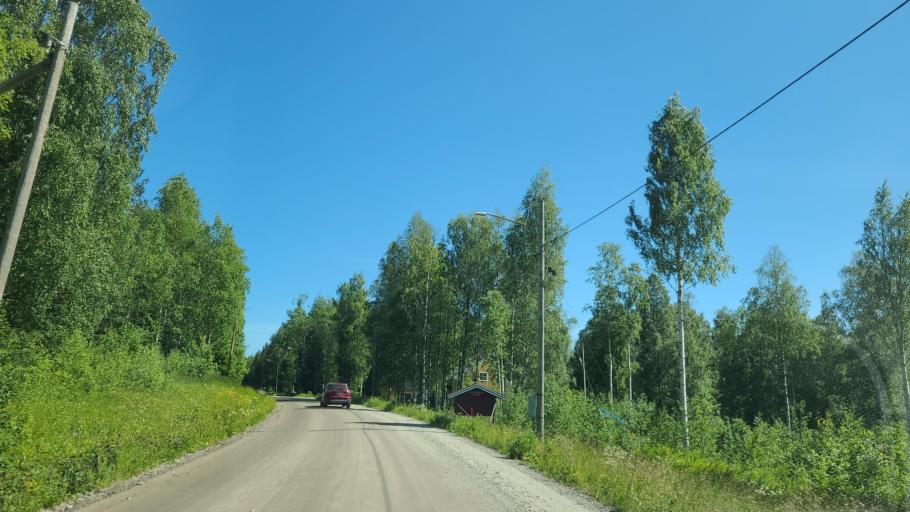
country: SE
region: Vaesterbotten
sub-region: Bjurholms Kommun
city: Bjurholm
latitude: 63.6857
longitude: 18.9645
